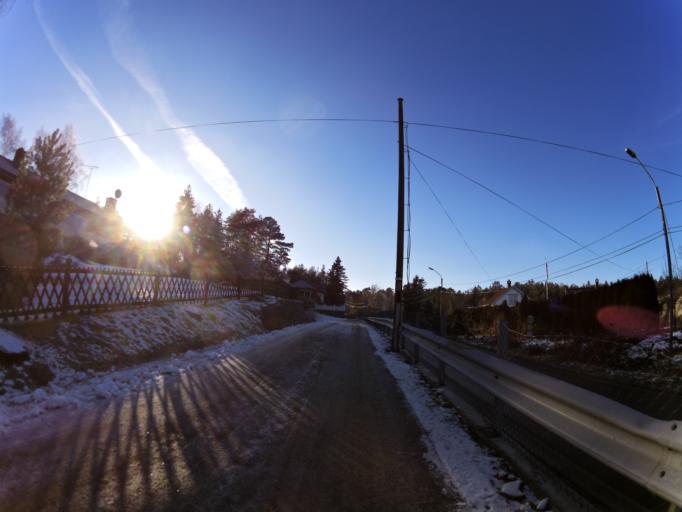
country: NO
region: Ostfold
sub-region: Fredrikstad
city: Fredrikstad
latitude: 59.2017
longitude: 10.8746
